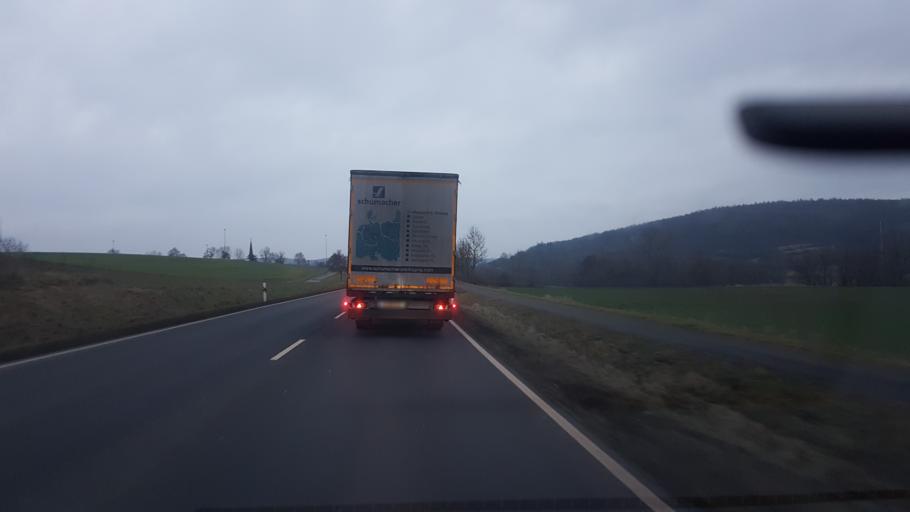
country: DE
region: Bavaria
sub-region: Regierungsbezirk Unterfranken
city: Rentweinsdorf
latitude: 50.0770
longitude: 10.7922
